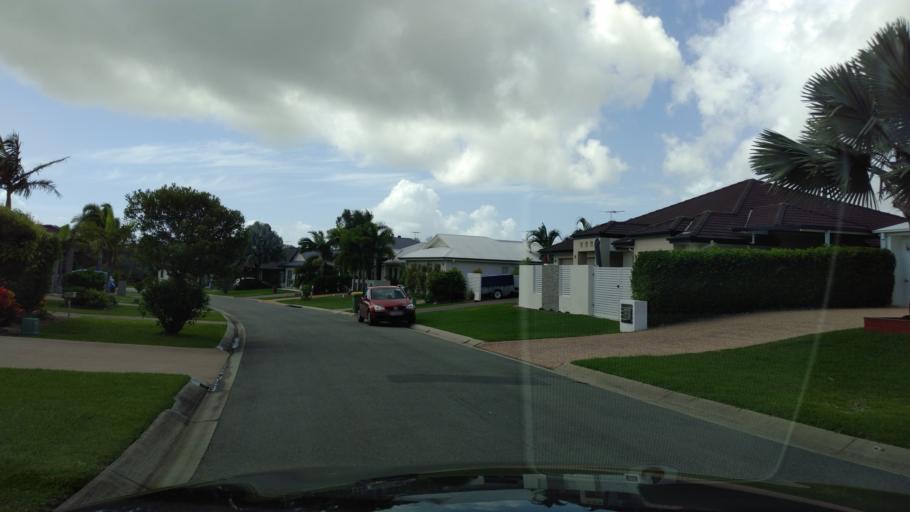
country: AU
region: Queensland
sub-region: Moreton Bay
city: Deception Bay
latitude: -27.2117
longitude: 153.0242
